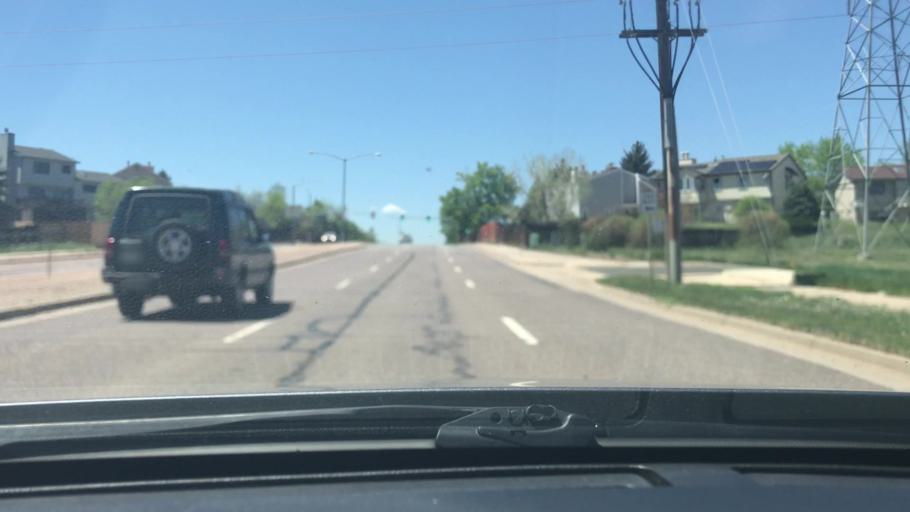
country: US
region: Colorado
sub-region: Arapahoe County
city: Dove Valley
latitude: 39.6531
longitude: -104.7536
